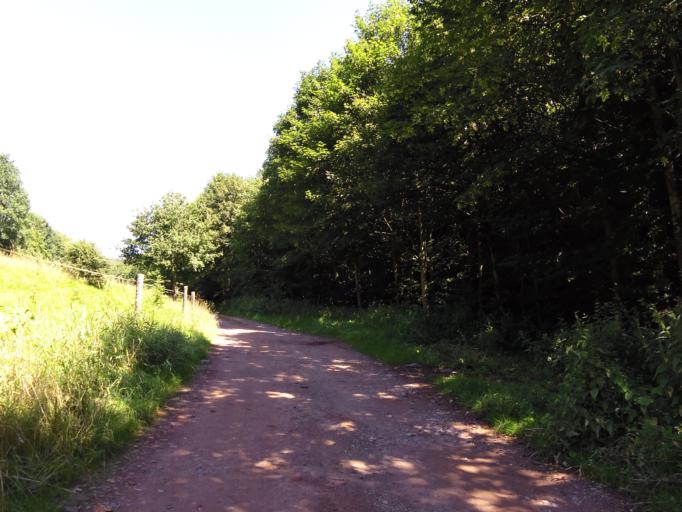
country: DE
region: Thuringia
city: Seebach
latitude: 50.9482
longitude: 10.4347
